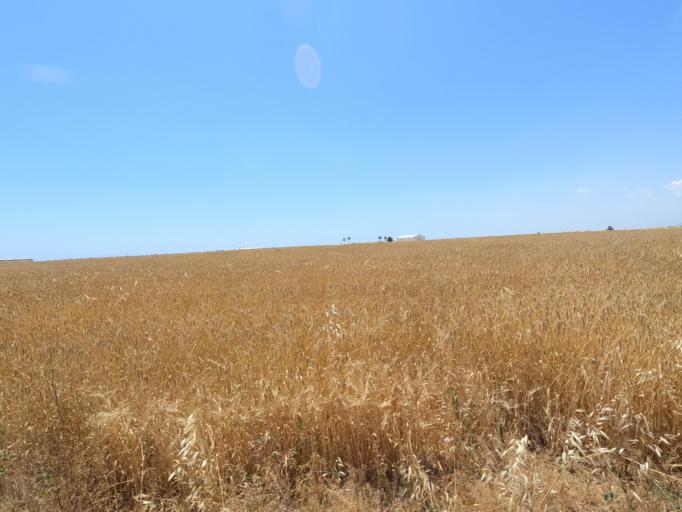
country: CY
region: Larnaka
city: Xylotymbou
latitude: 35.0199
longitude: 33.7249
